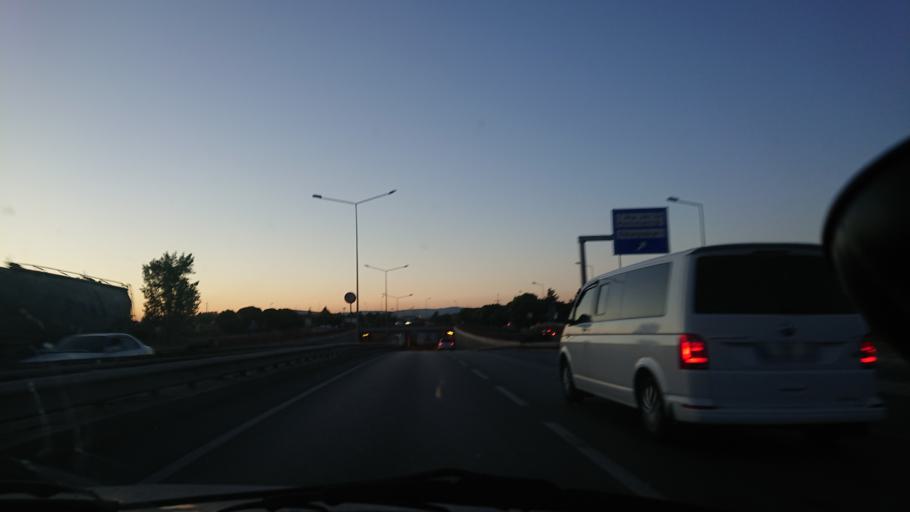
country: TR
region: Eskisehir
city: Eskisehir
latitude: 39.7723
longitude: 30.5588
